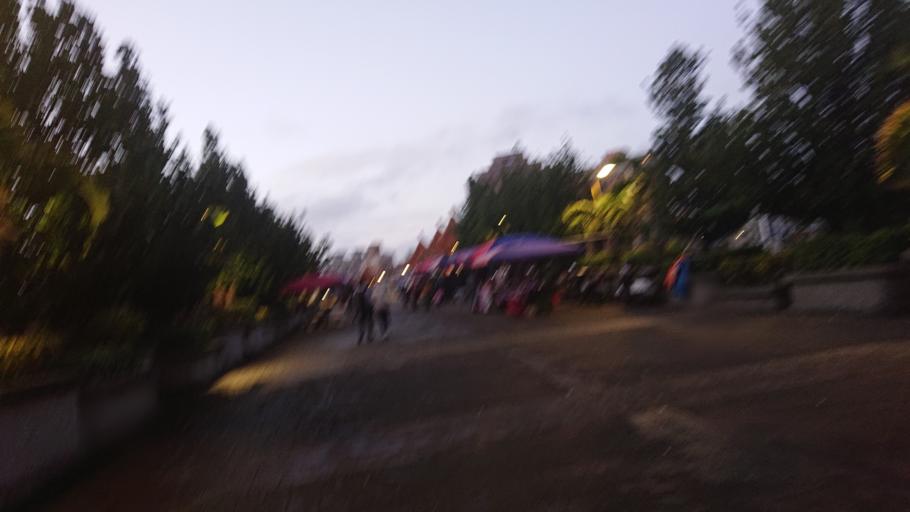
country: TW
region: Taiwan
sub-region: Taoyuan
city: Taoyuan
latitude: 24.9323
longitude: 121.3722
